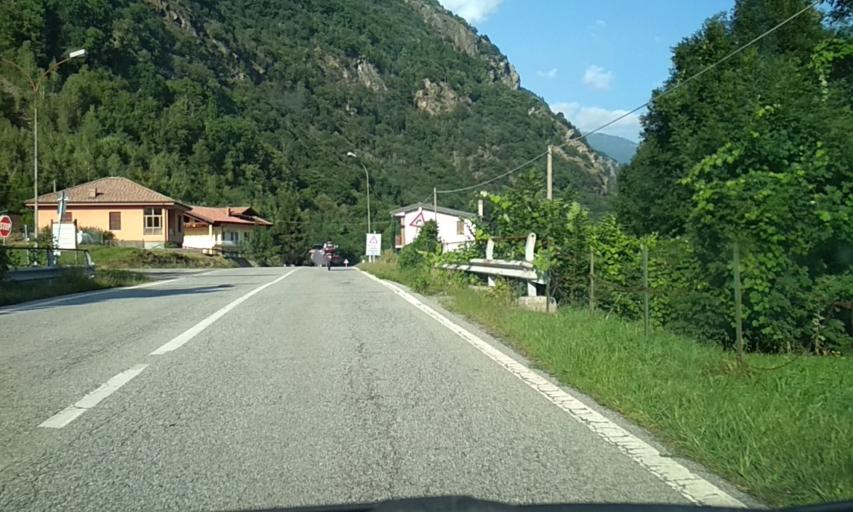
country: IT
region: Piedmont
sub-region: Provincia di Torino
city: Sparone
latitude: 45.4178
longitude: 7.5599
